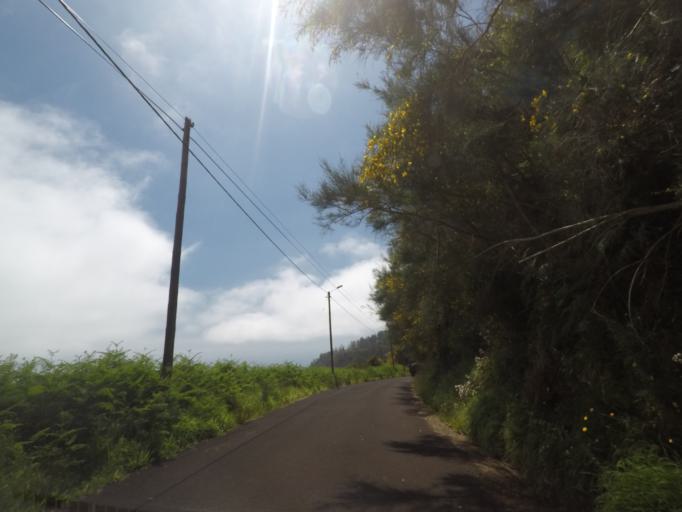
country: PT
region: Madeira
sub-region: Calheta
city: Arco da Calheta
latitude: 32.7281
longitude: -17.1265
